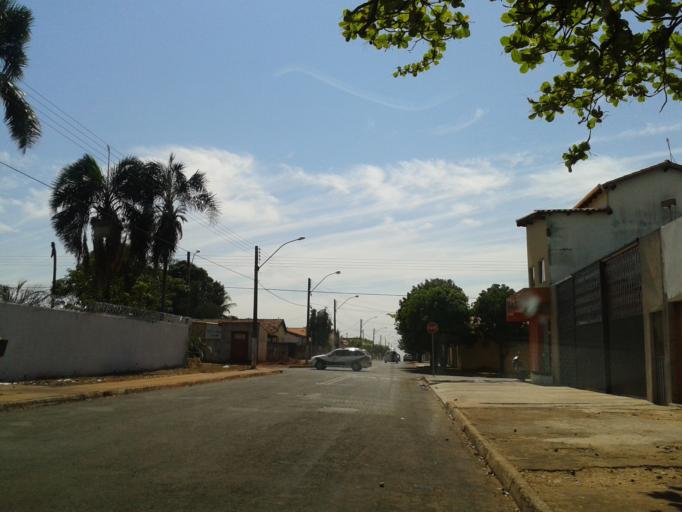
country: BR
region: Minas Gerais
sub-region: Santa Vitoria
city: Santa Vitoria
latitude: -18.9963
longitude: -50.5441
